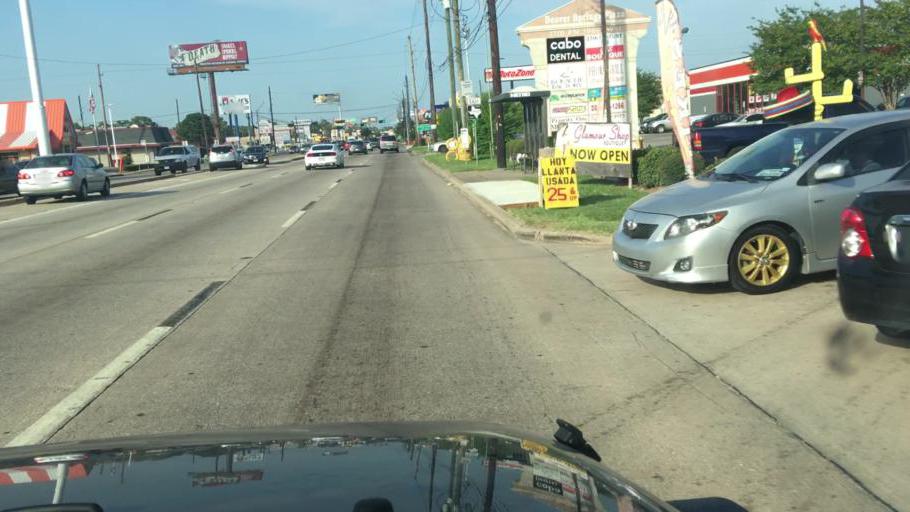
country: US
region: Texas
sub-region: Harris County
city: Spring
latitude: 30.0118
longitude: -95.4548
